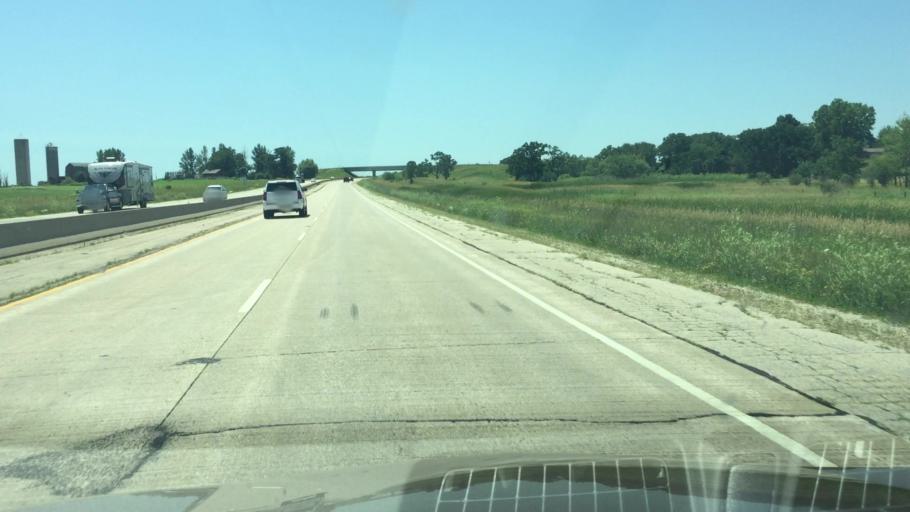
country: US
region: Wisconsin
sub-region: Fond du Lac County
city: Waupun
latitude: 43.5881
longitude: -88.7447
